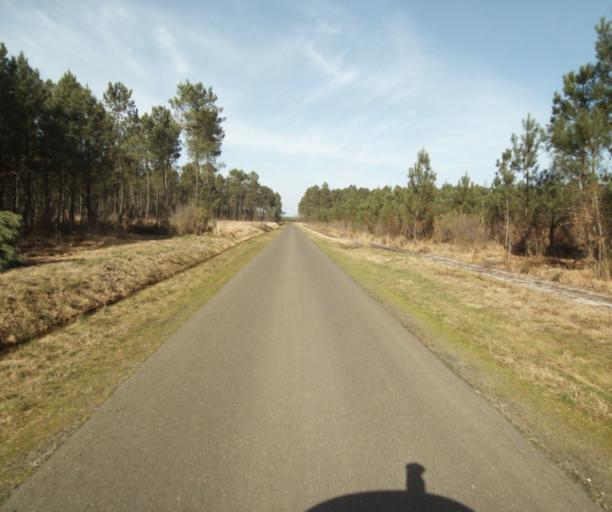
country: FR
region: Aquitaine
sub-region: Departement des Landes
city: Roquefort
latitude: 44.2081
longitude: -0.2013
